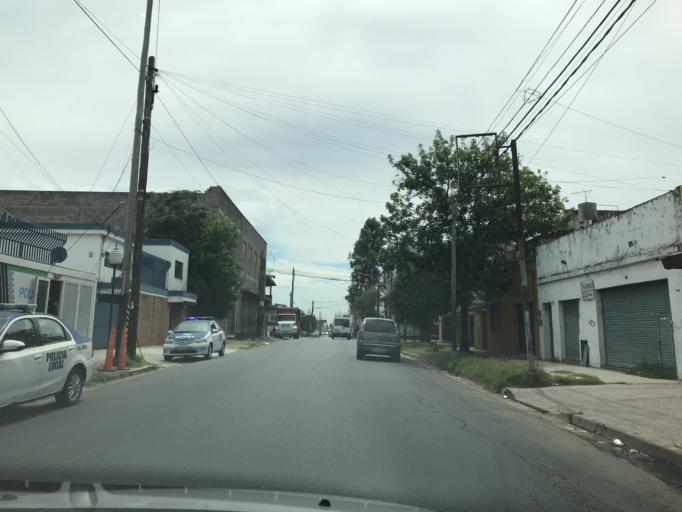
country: AR
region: Buenos Aires
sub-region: Partido de Lomas de Zamora
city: Lomas de Zamora
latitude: -34.7309
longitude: -58.4253
